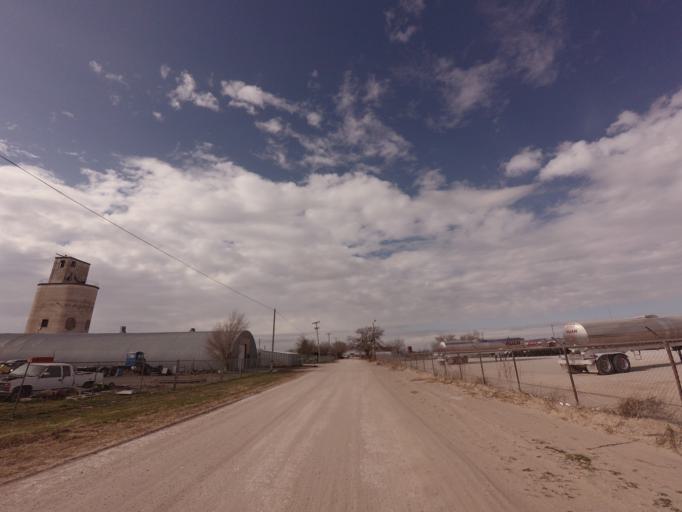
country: US
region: New Mexico
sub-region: Curry County
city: Clovis
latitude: 34.3919
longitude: -103.2186
